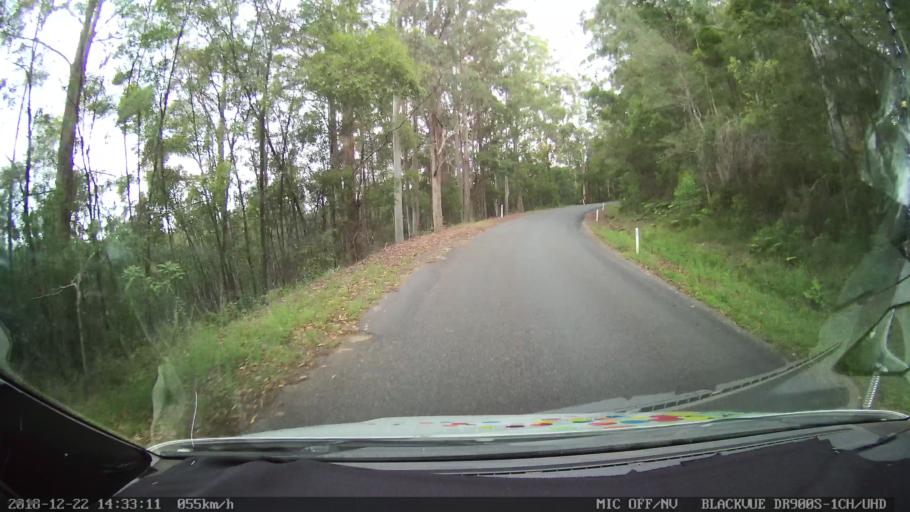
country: AU
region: New South Wales
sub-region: Bellingen
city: Dorrigo
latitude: -30.1109
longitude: 152.6242
